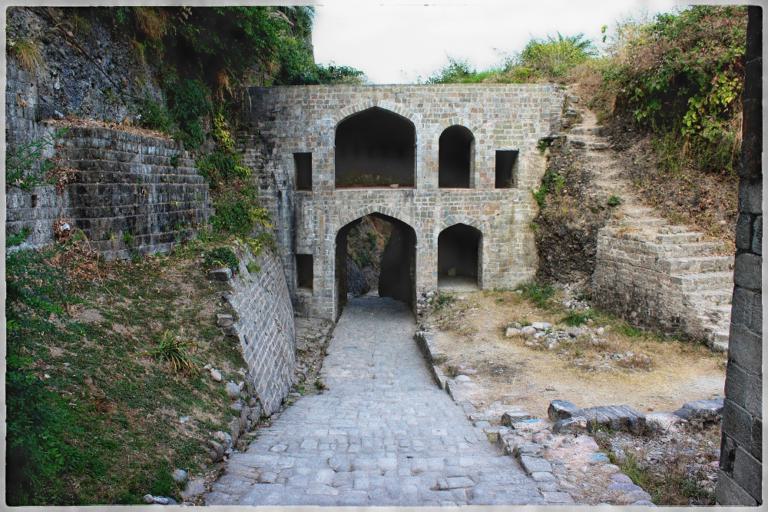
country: IN
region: Himachal Pradesh
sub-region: Kangra
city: Kangra
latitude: 32.0872
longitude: 76.2548
